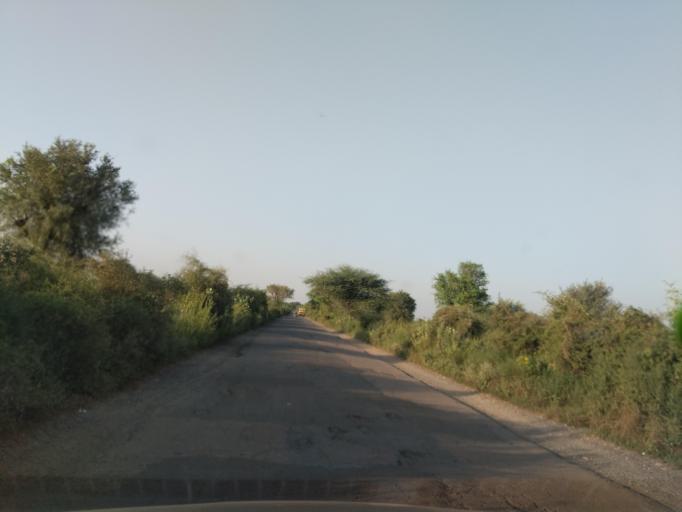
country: IN
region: Rajasthan
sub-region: Churu
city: Rajgarh
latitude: 28.5800
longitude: 75.3722
